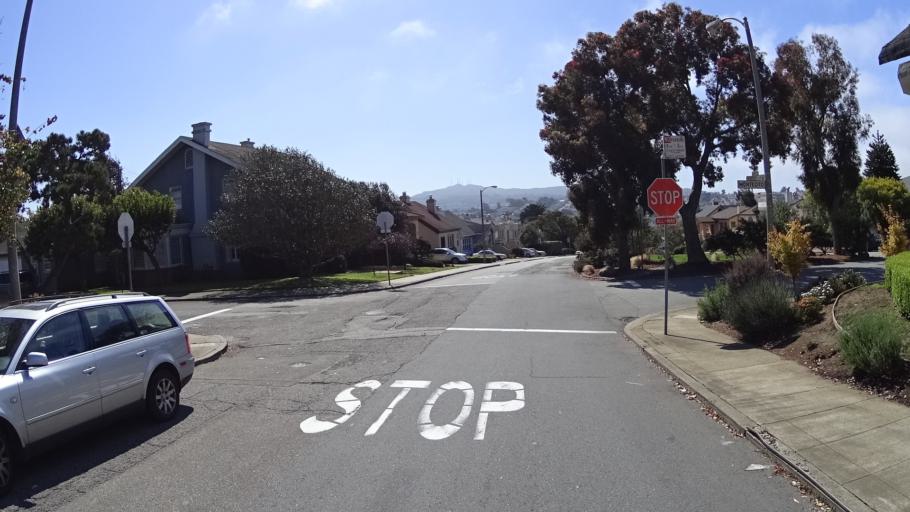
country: US
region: California
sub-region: San Mateo County
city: Daly City
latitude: 37.7299
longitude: -122.4565
